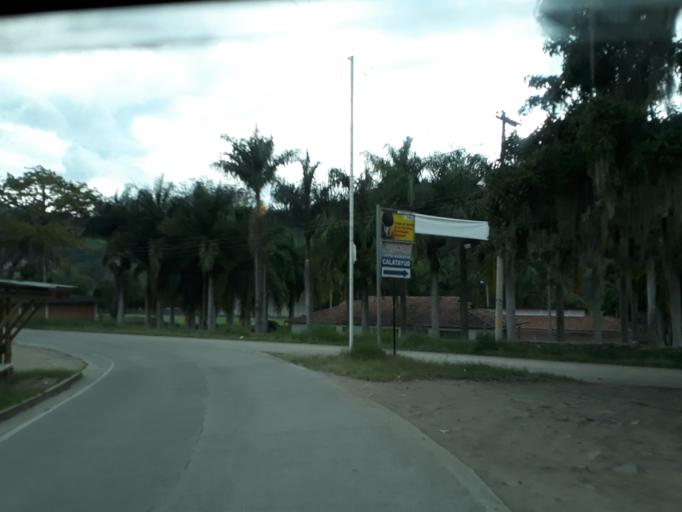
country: CO
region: Cundinamarca
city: Pacho
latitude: 5.1508
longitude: -74.1534
